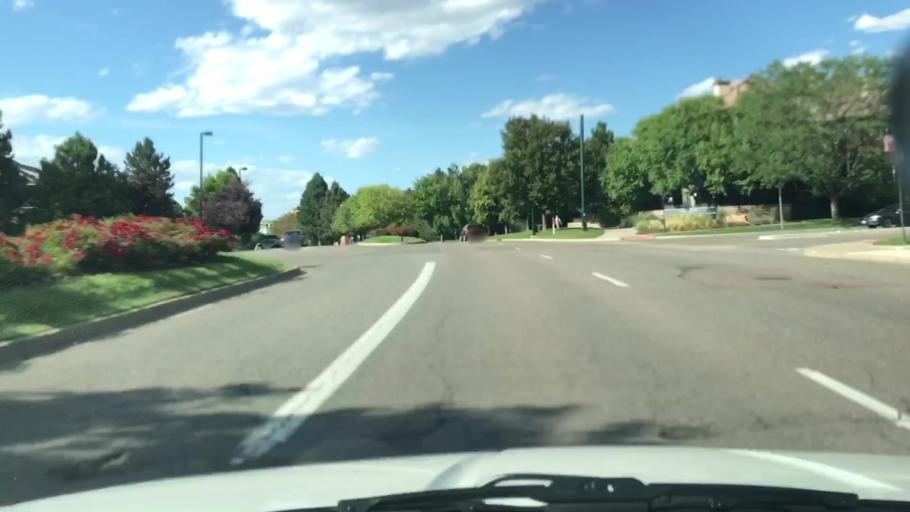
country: US
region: Colorado
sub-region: Arapahoe County
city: Greenwood Village
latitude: 39.6320
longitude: -104.9109
